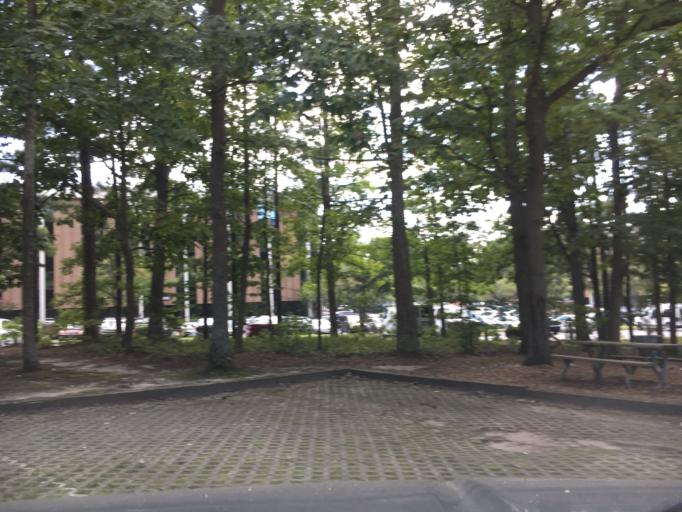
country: US
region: Virginia
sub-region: Henrico County
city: Tuckahoe
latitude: 37.6050
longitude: -77.5444
